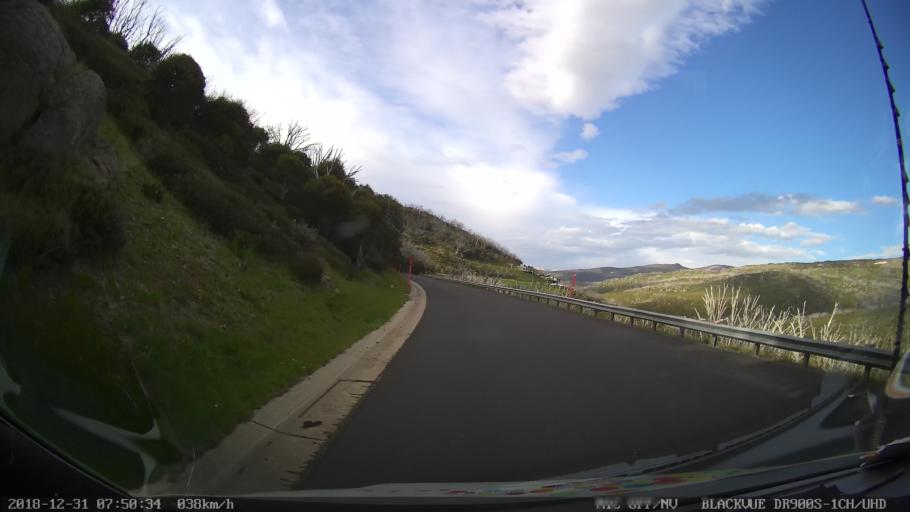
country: AU
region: New South Wales
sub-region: Snowy River
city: Jindabyne
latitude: -36.3745
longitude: 148.3797
